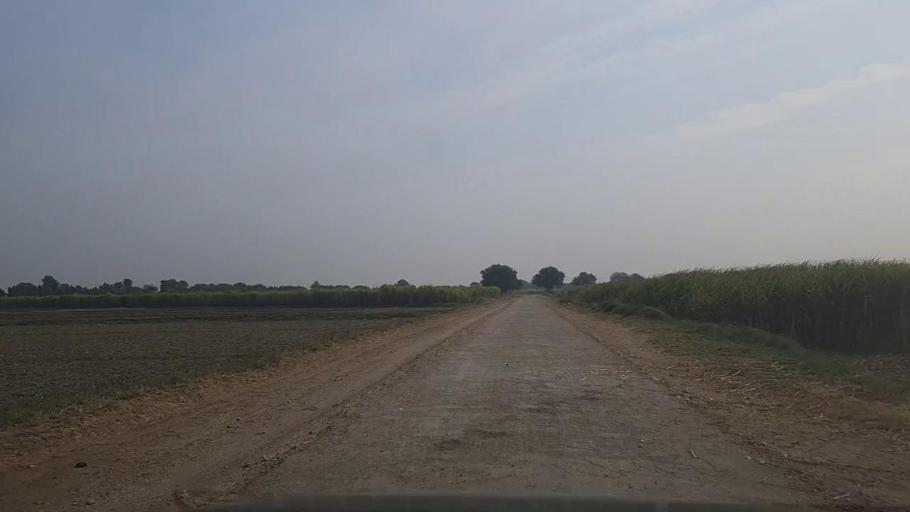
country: PK
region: Sindh
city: Bulri
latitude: 25.0249
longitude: 68.2930
